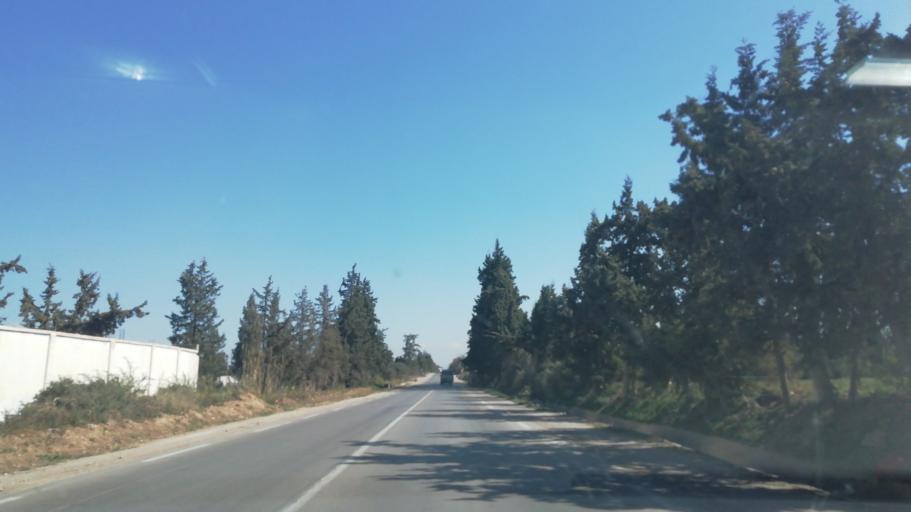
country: DZ
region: Mascara
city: Sig
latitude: 35.5653
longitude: -0.0834
